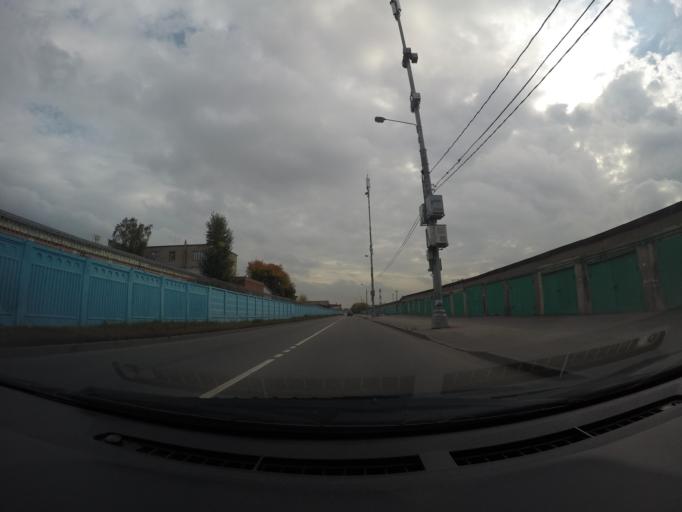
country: RU
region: Moscow
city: Lefortovo
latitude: 55.7719
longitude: 37.7178
